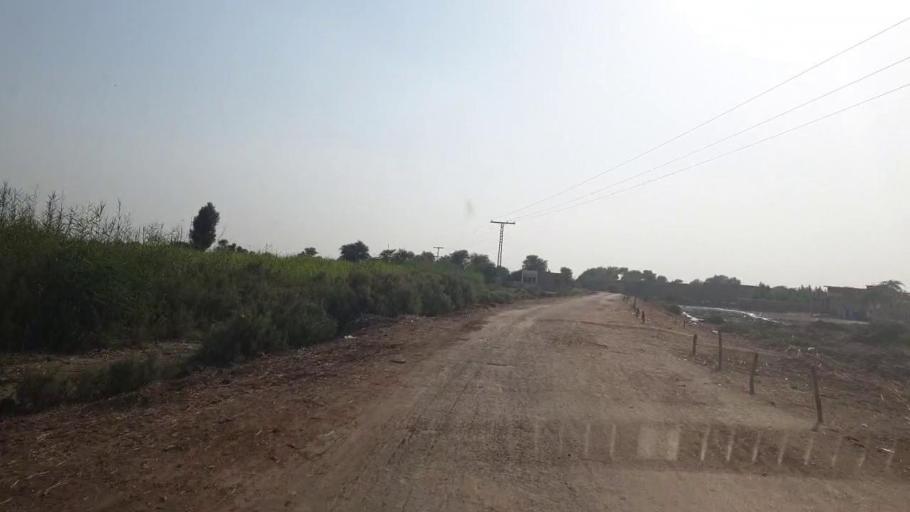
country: PK
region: Sindh
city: Sanghar
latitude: 26.0404
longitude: 68.8973
